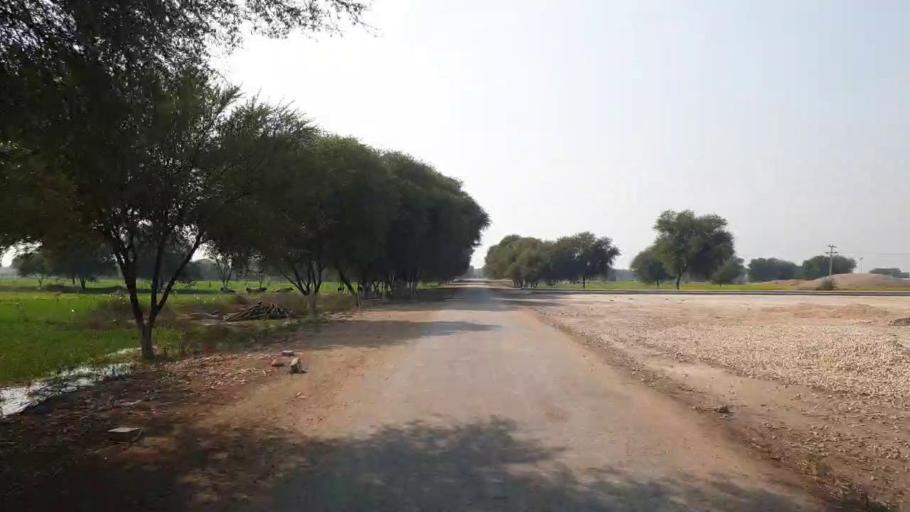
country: PK
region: Sindh
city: Mirwah Gorchani
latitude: 25.3535
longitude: 68.9371
